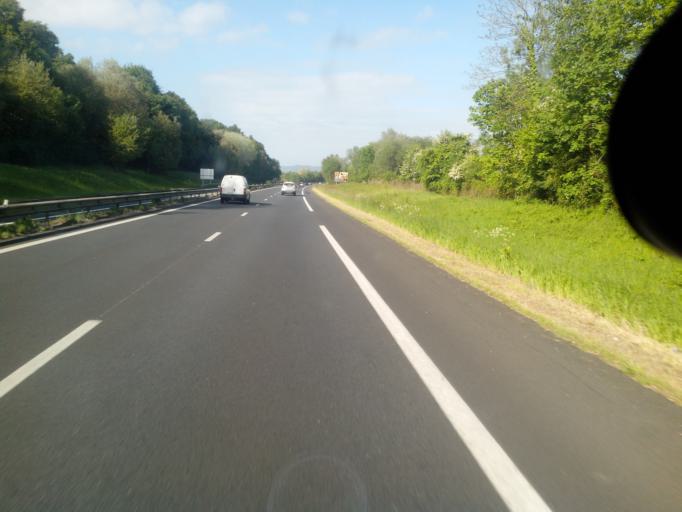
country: FR
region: Lower Normandy
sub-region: Departement du Calvados
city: Troarn
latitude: 49.1955
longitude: -0.1841
